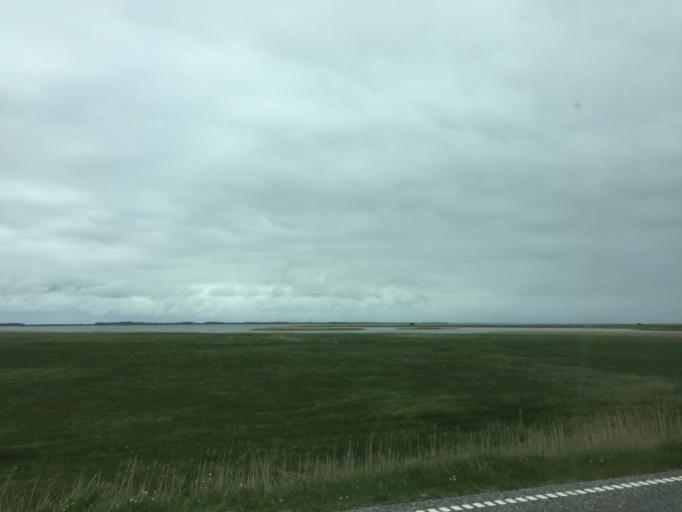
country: DK
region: Central Jutland
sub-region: Lemvig Kommune
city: Harboore
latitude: 56.4013
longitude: 8.1218
